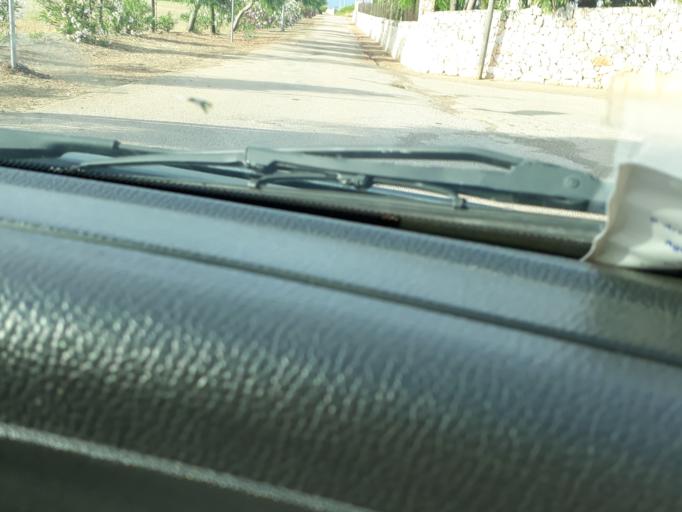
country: IT
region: Apulia
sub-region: Provincia di Brindisi
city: Carovigno
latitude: 40.7624
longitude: 17.6853
